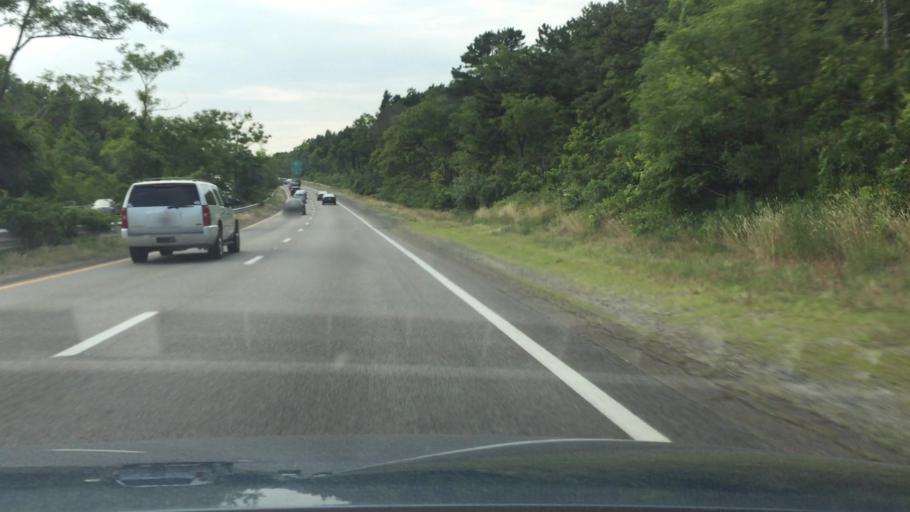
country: US
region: Massachusetts
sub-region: Barnstable County
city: Sagamore
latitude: 41.7556
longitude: -70.5210
